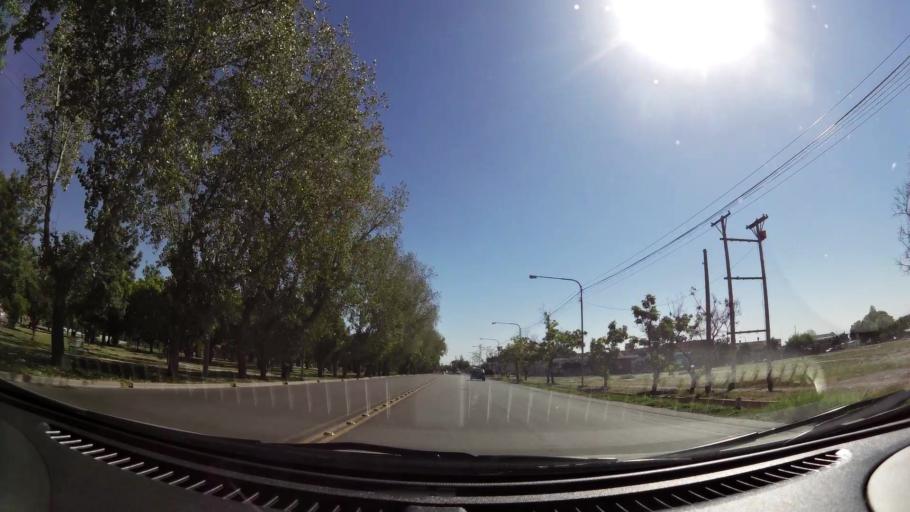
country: AR
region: Mendoza
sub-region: Departamento de Maipu
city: Maipu
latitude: -32.9723
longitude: -68.7935
